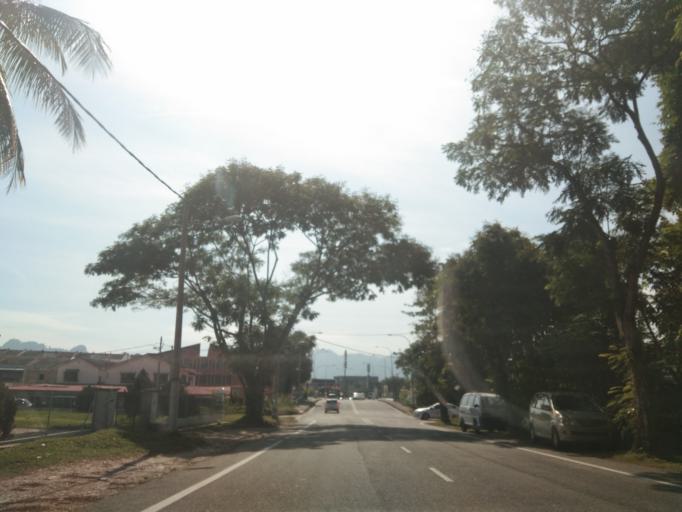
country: MY
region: Perak
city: Ipoh
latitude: 4.5715
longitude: 101.1104
